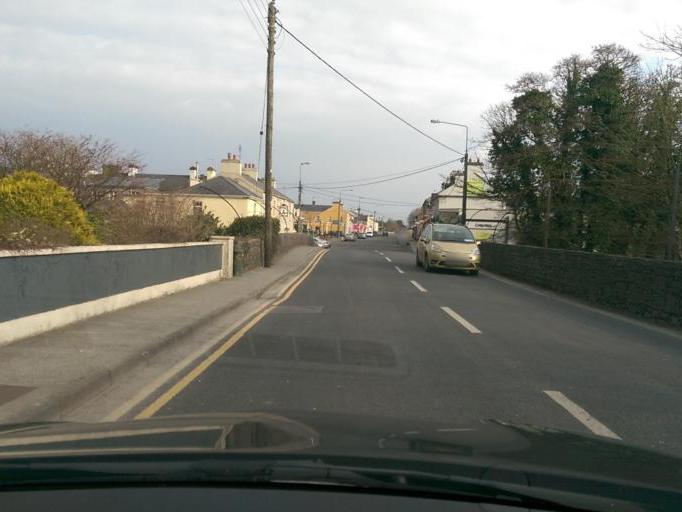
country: IE
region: Connaught
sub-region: County Galway
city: Loughrea
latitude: 53.4703
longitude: -8.5024
